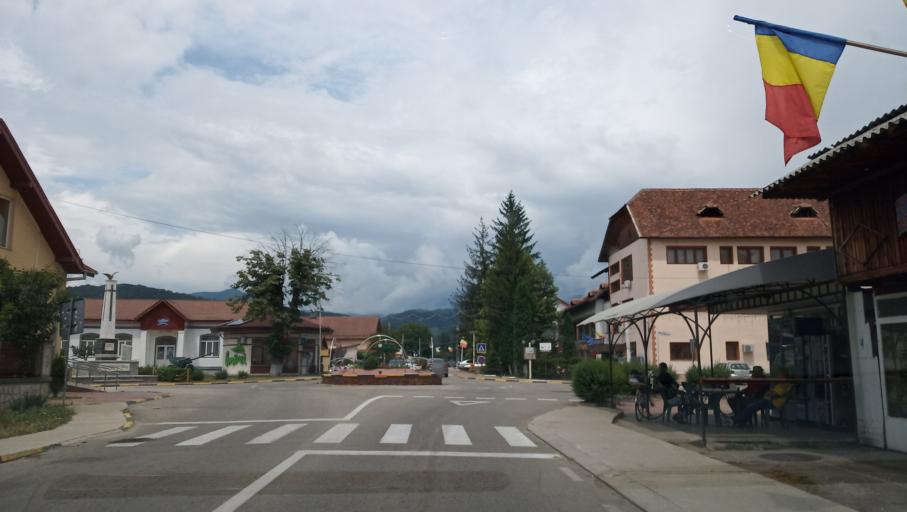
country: RO
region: Gorj
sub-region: Comuna Tismana
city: Tismana
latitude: 45.0496
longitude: 22.9472
